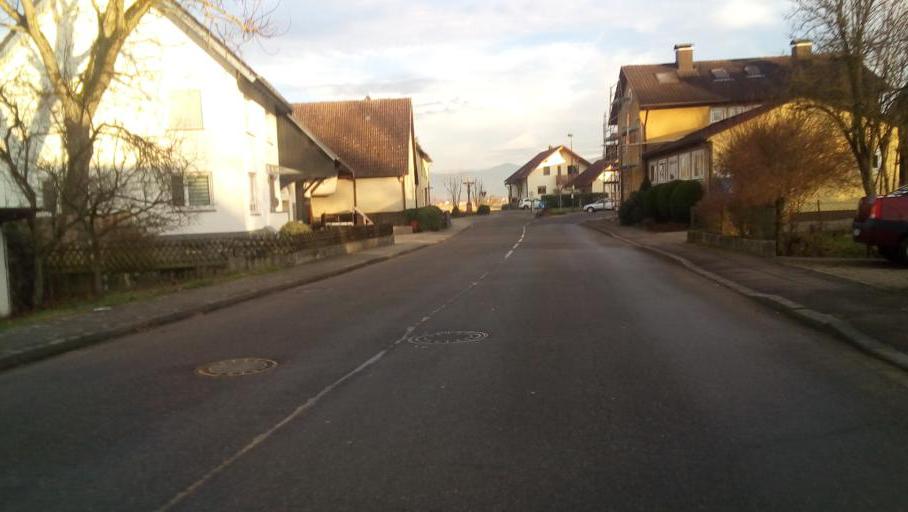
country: DE
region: Baden-Wuerttemberg
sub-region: Karlsruhe Region
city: Zell
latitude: 48.6646
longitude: 8.0178
